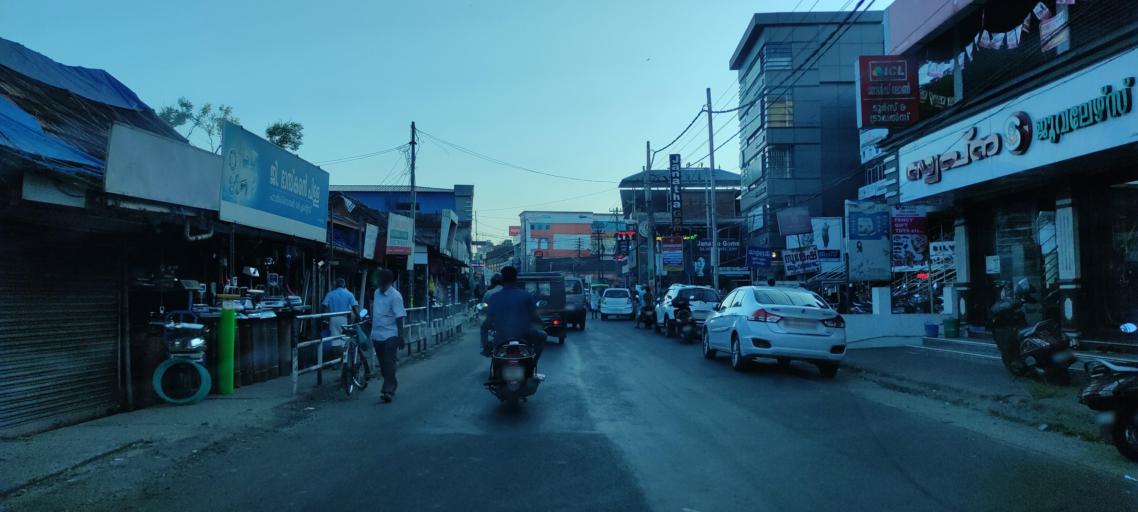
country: IN
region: Kerala
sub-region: Alappuzha
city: Kayankulam
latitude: 9.1745
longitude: 76.5013
